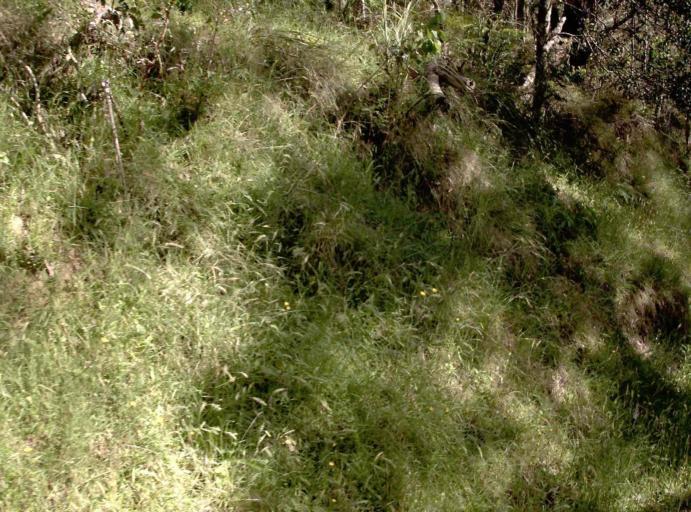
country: AU
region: New South Wales
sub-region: Bombala
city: Bombala
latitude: -37.3648
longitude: 148.6844
